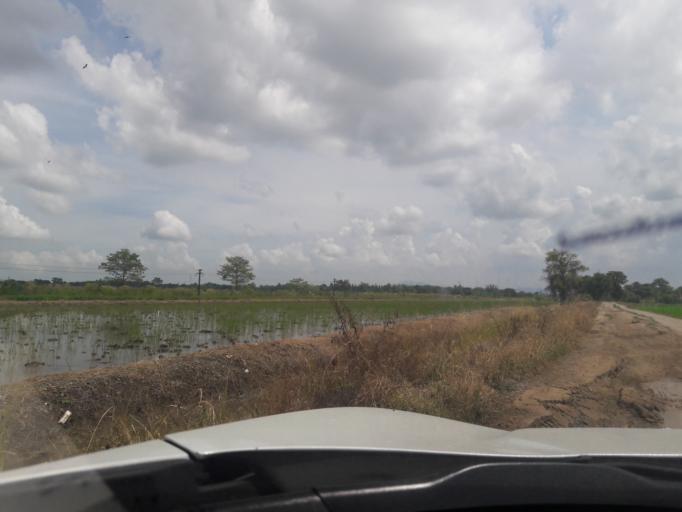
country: TH
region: Lop Buri
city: Ban Mi
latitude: 15.0515
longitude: 100.5277
